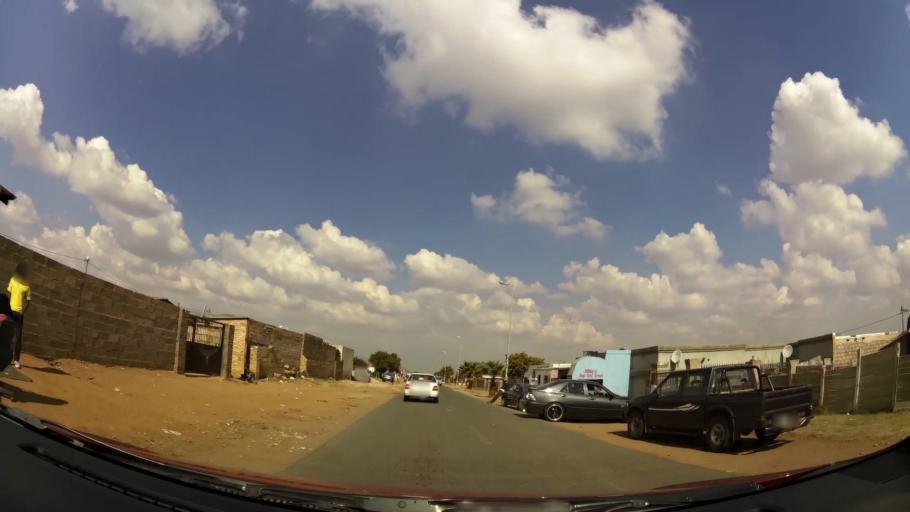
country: ZA
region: Gauteng
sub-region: City of Johannesburg Metropolitan Municipality
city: Roodepoort
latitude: -26.1910
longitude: 27.8680
